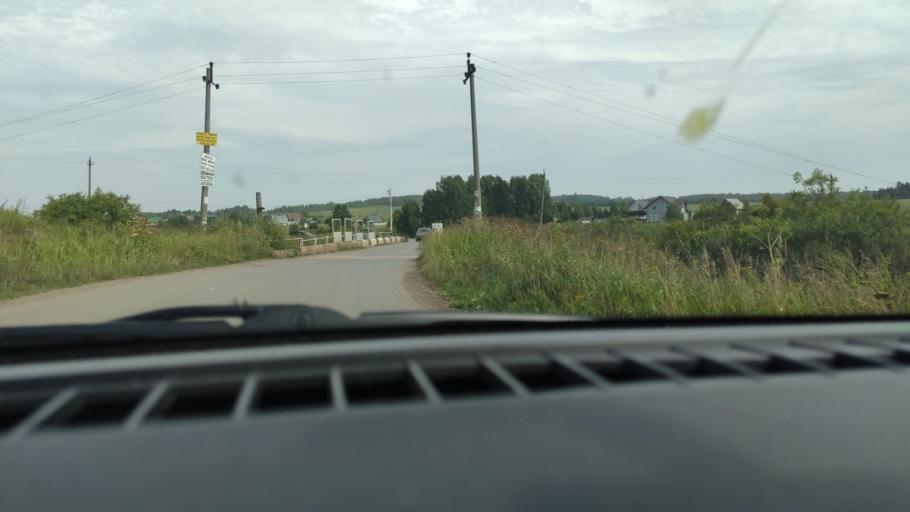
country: RU
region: Perm
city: Bershet'
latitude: 57.7541
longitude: 56.3775
